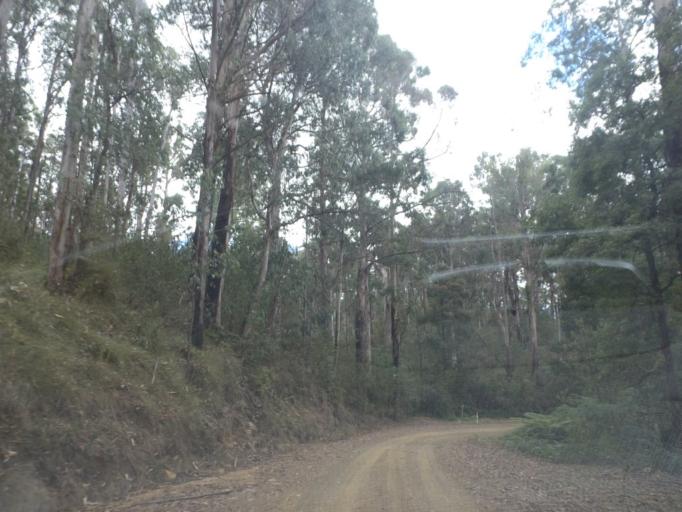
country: AU
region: Victoria
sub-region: Murrindindi
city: Alexandra
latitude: -37.4225
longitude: 145.9711
